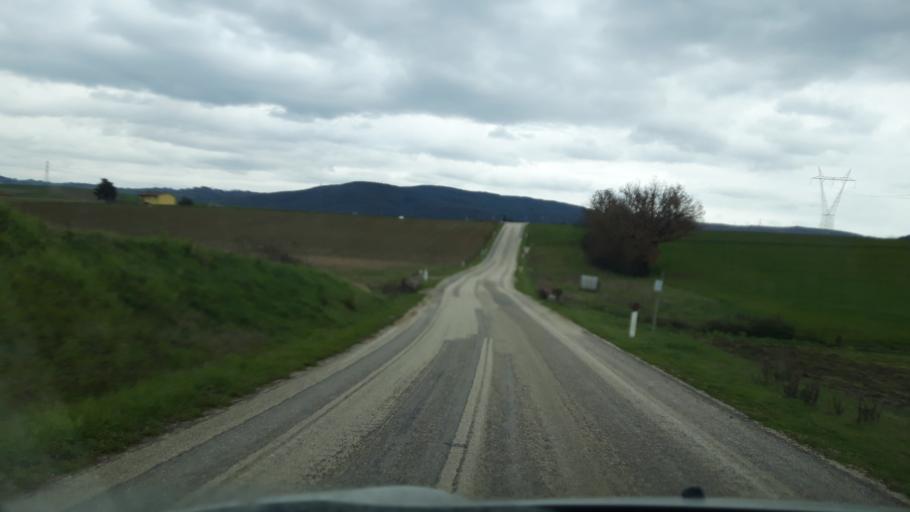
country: IT
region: Umbria
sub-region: Provincia di Perugia
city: Tavernelle
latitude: 42.9885
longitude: 12.1777
